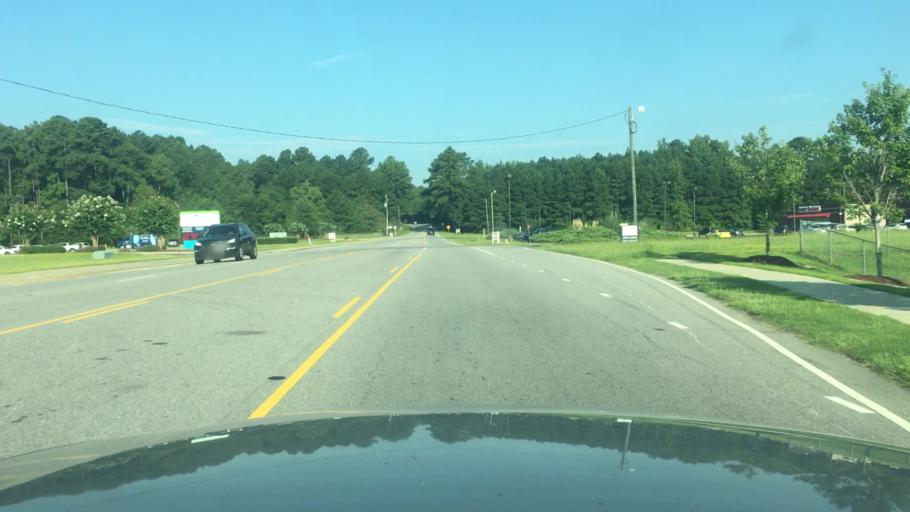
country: US
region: North Carolina
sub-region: Cumberland County
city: Eastover
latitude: 35.1577
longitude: -78.8701
